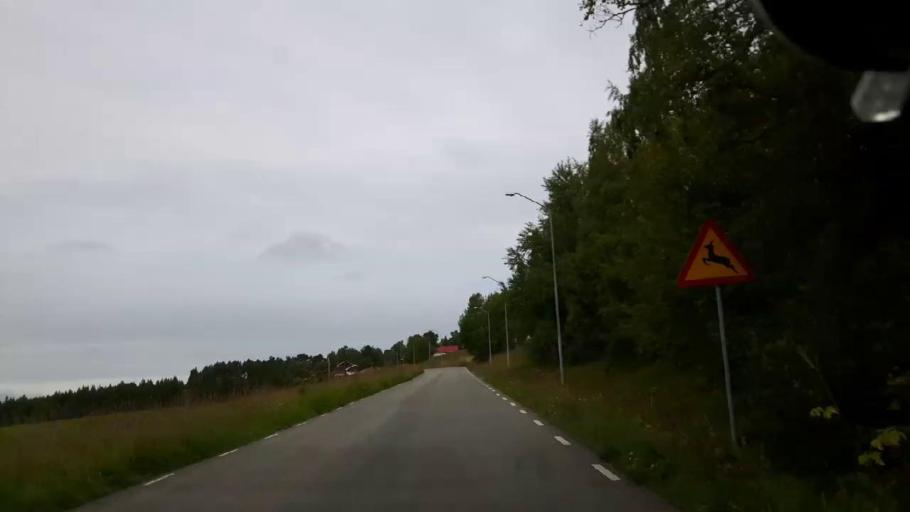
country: SE
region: Jaemtland
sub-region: OEstersunds Kommun
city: Ostersund
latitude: 63.1673
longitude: 14.5251
